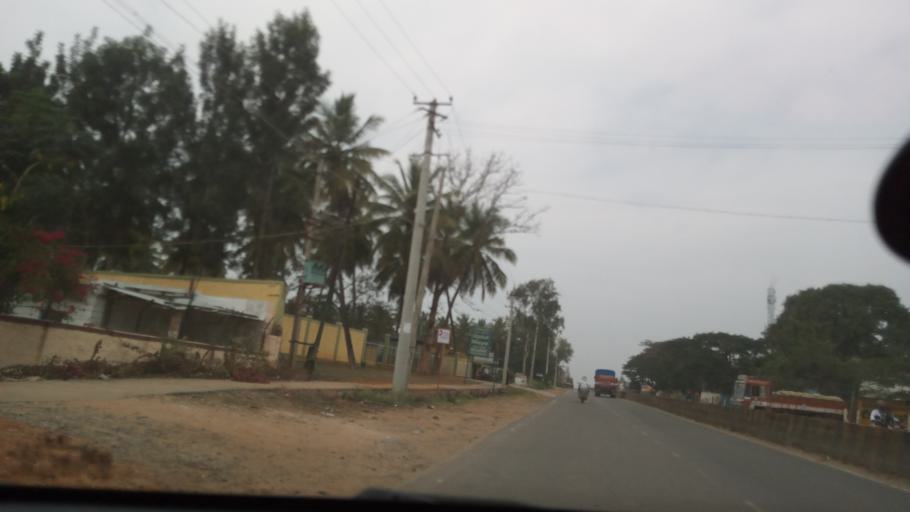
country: IN
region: Karnataka
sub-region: Chamrajnagar
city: Chamrajnagar
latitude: 11.9045
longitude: 76.9472
